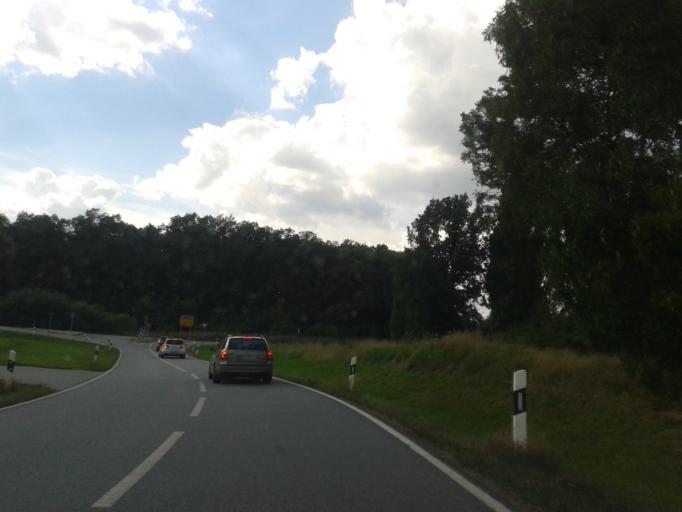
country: DE
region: Saxony
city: Radibor
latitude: 51.2050
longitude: 14.3754
